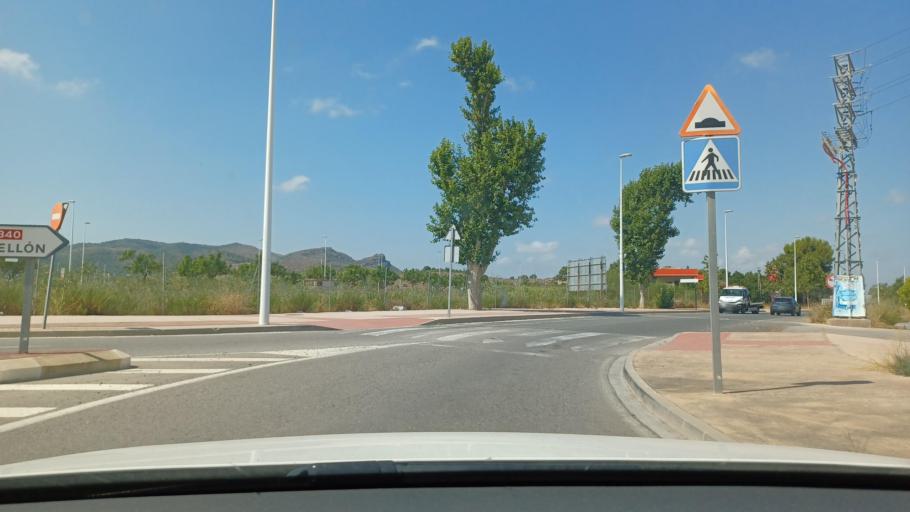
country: ES
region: Valencia
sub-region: Provincia de Valencia
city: Sagunto
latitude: 39.6832
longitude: -0.2680
